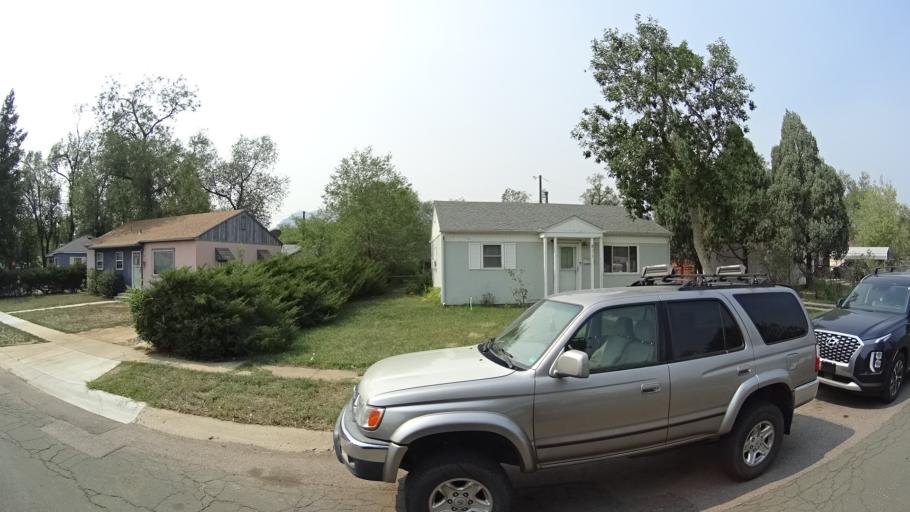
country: US
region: Colorado
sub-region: El Paso County
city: Colorado Springs
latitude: 38.8077
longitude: -104.8166
